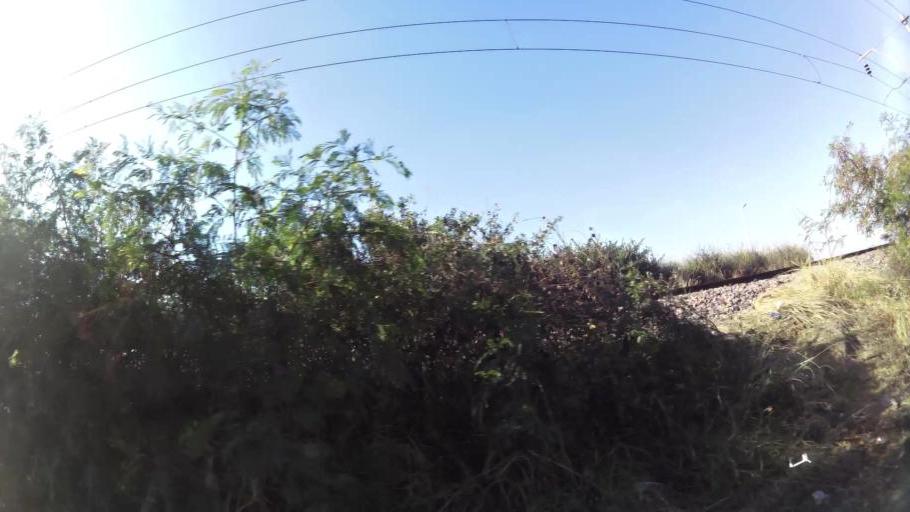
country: ZA
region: North-West
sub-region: Bojanala Platinum District Municipality
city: Rustenburg
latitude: -25.6491
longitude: 27.2369
